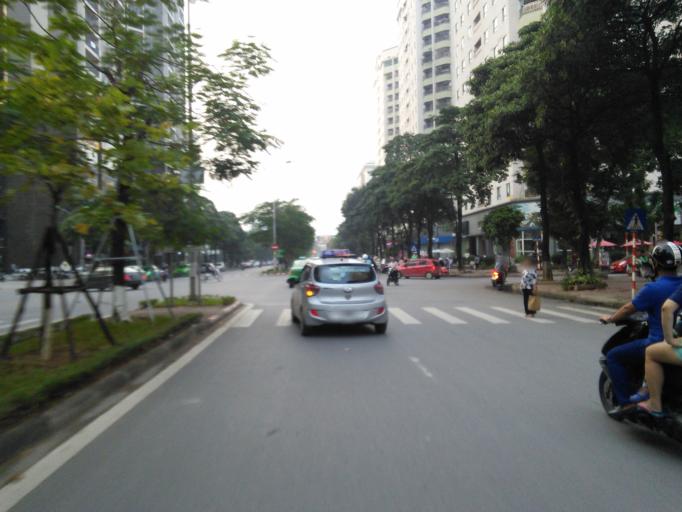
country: VN
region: Ha Noi
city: Thanh Xuan
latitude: 21.0083
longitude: 105.8017
